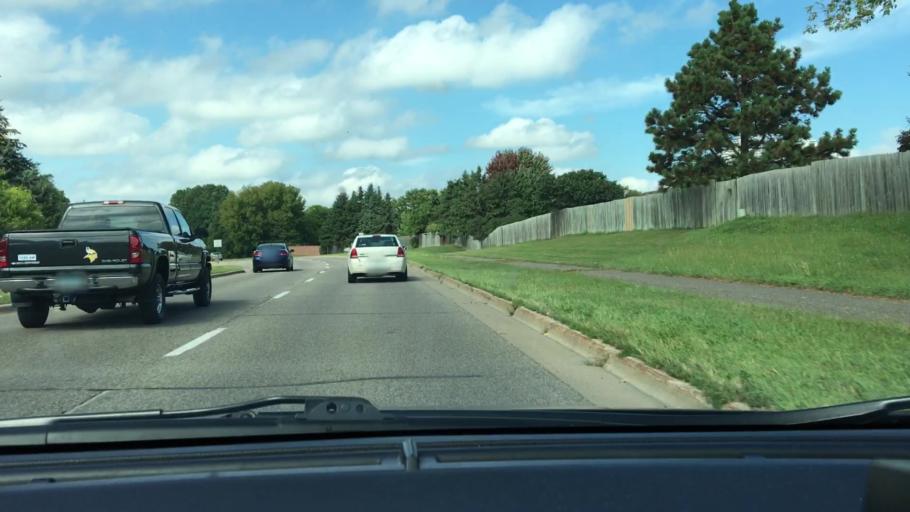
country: US
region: Minnesota
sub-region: Hennepin County
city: Maple Grove
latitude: 45.0612
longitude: -93.4327
